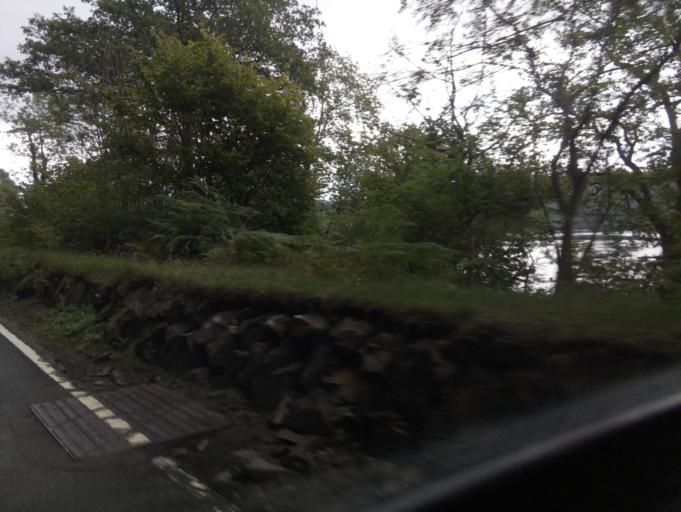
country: GB
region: Scotland
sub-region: Highland
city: Beauly
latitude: 57.2634
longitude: -4.5179
